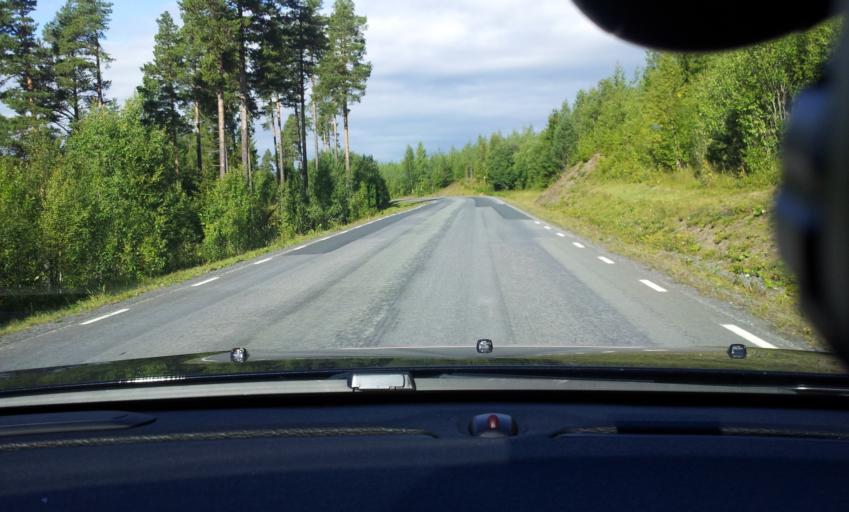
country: SE
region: Jaemtland
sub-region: Are Kommun
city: Jarpen
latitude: 63.2900
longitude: 13.7286
